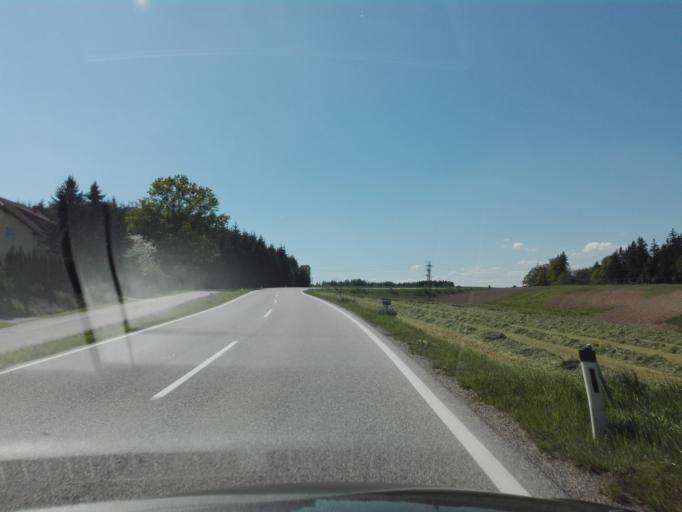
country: AT
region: Upper Austria
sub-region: Politischer Bezirk Grieskirchen
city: Bad Schallerbach
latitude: 48.3225
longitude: 13.8803
